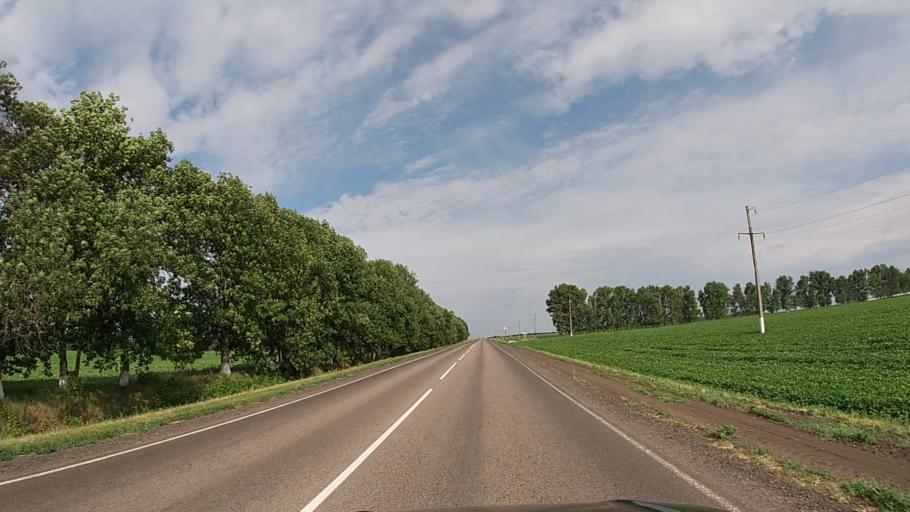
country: RU
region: Belgorod
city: Krasnaya Yaruga
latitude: 50.8050
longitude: 35.5487
